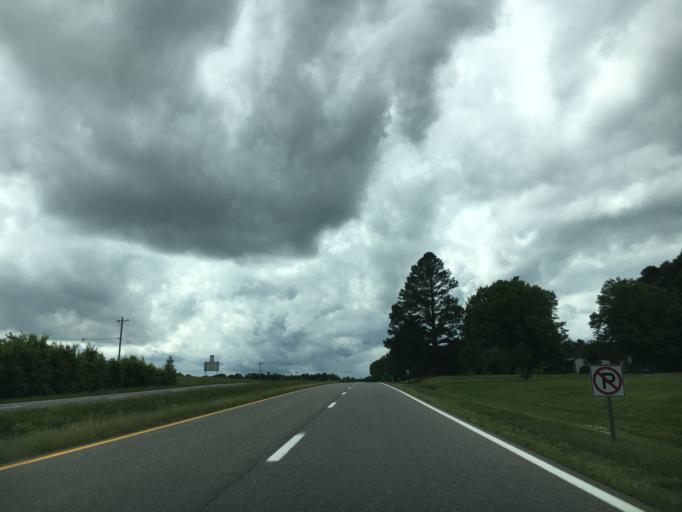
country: US
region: Virginia
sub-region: Mecklenburg County
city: Clarksville
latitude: 36.6615
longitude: -78.7108
